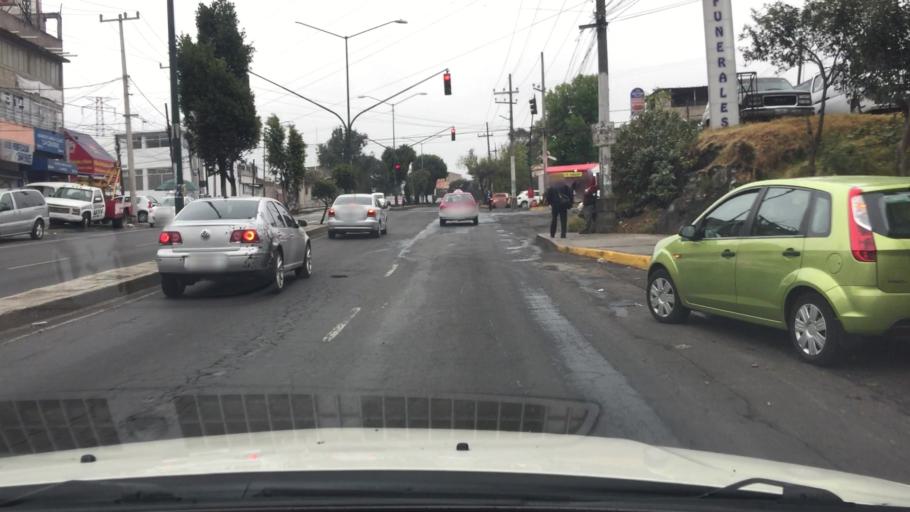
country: MX
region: Mexico City
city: Tlalpan
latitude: 19.2744
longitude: -99.2073
